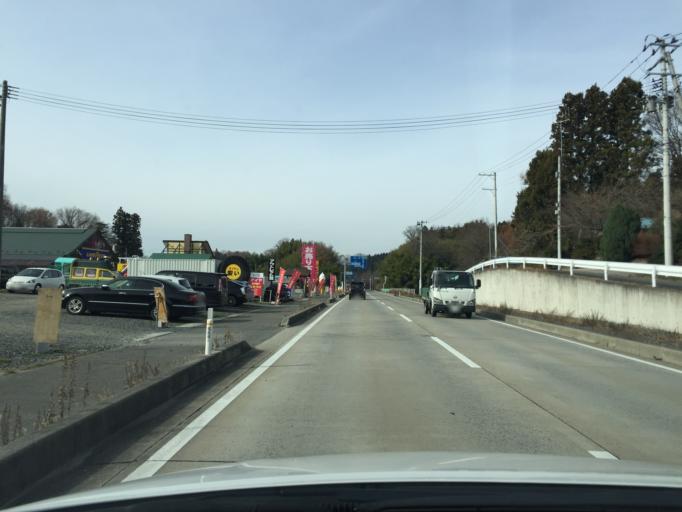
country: JP
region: Fukushima
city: Funehikimachi-funehiki
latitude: 37.4442
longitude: 140.5348
